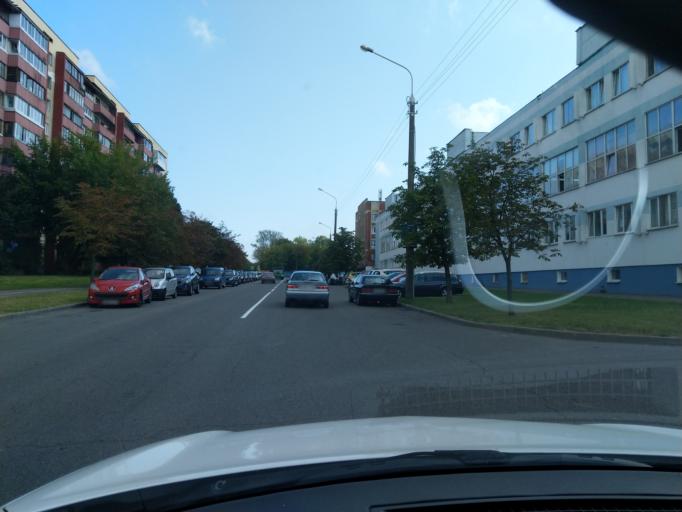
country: BY
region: Minsk
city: Minsk
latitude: 53.8945
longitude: 27.5870
